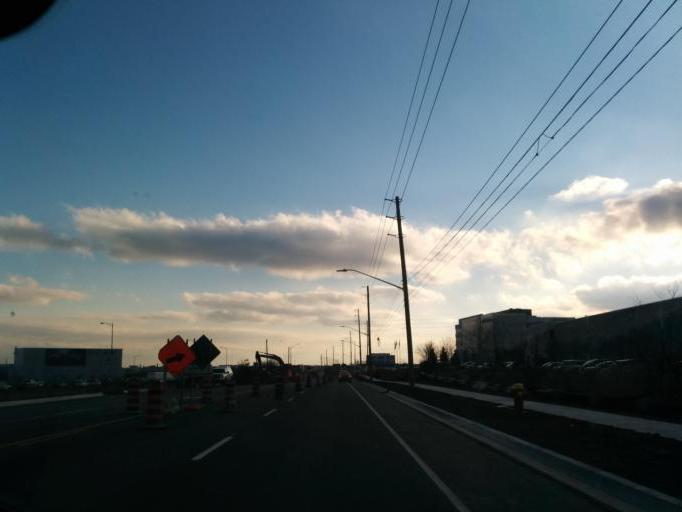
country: CA
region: Ontario
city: Oakville
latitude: 43.4907
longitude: -79.6743
